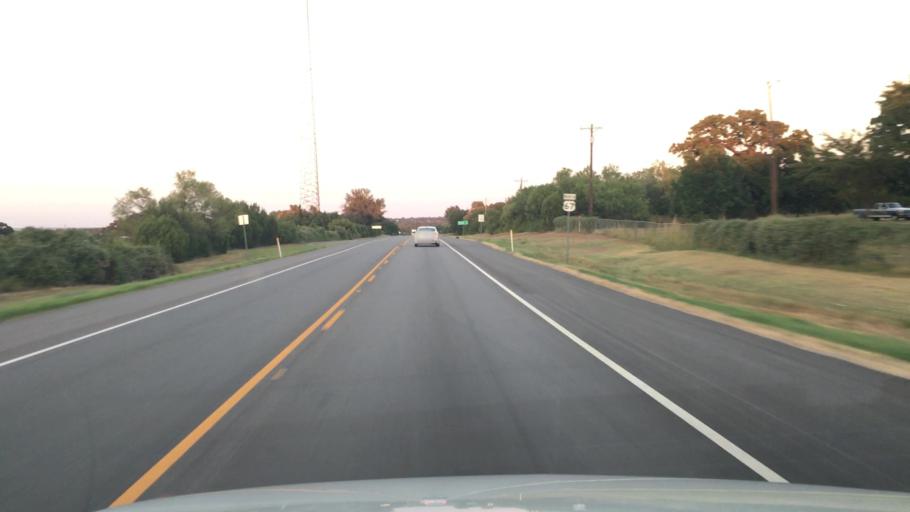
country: US
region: Texas
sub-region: Somervell County
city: Glen Rose
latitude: 32.1917
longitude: -97.8366
